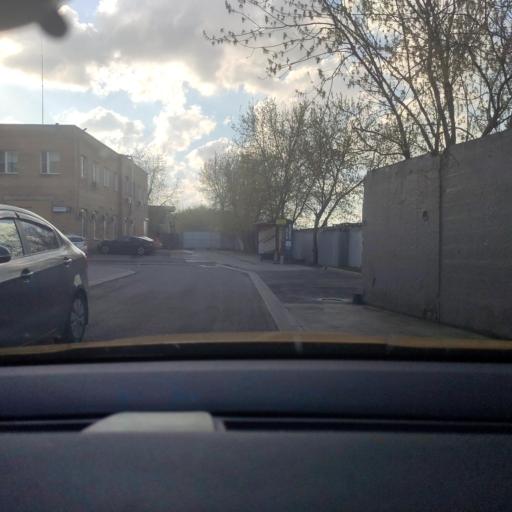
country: RU
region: Moscow
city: Kuz'minki
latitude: 55.6835
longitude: 37.7811
